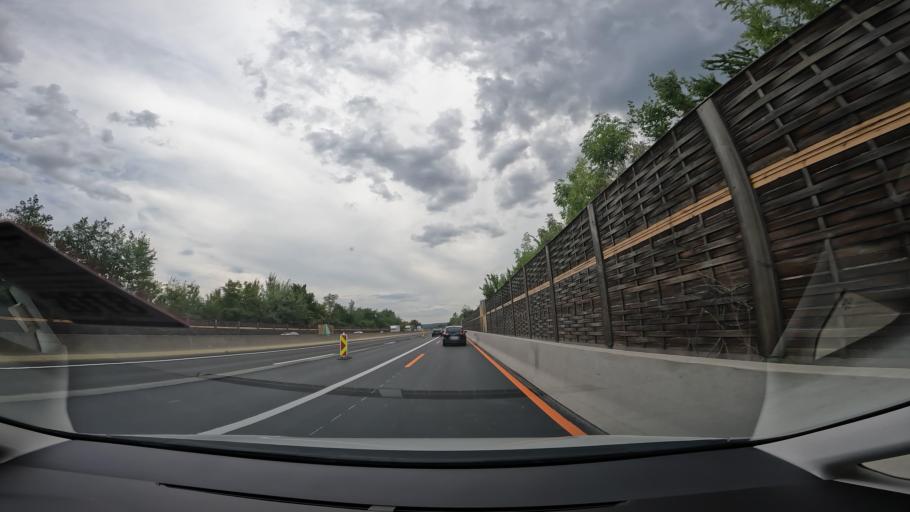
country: AT
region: Styria
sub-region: Politischer Bezirk Hartberg-Fuerstenfeld
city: Sankt Johann in der Haide
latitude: 47.2392
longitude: 15.9976
